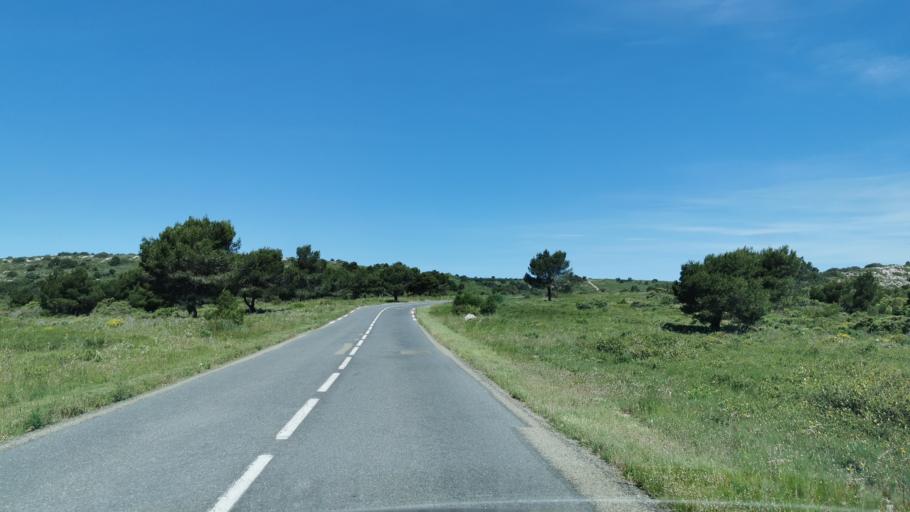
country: FR
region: Languedoc-Roussillon
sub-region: Departement de l'Aude
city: Armissan
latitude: 43.1624
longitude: 3.1354
